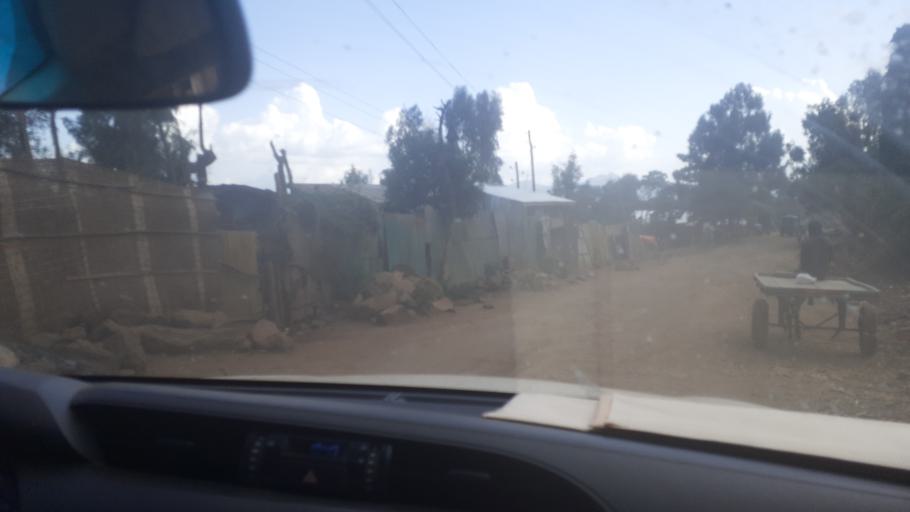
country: ET
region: Southern Nations, Nationalities, and People's Region
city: K'olito
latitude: 7.5406
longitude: 37.8464
